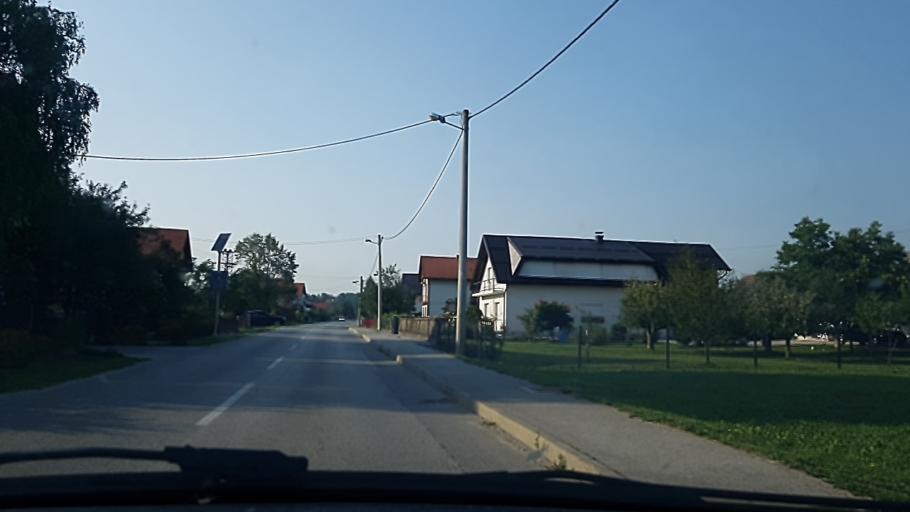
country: HR
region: Zagrebacka
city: Pojatno
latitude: 45.9347
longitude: 15.8141
